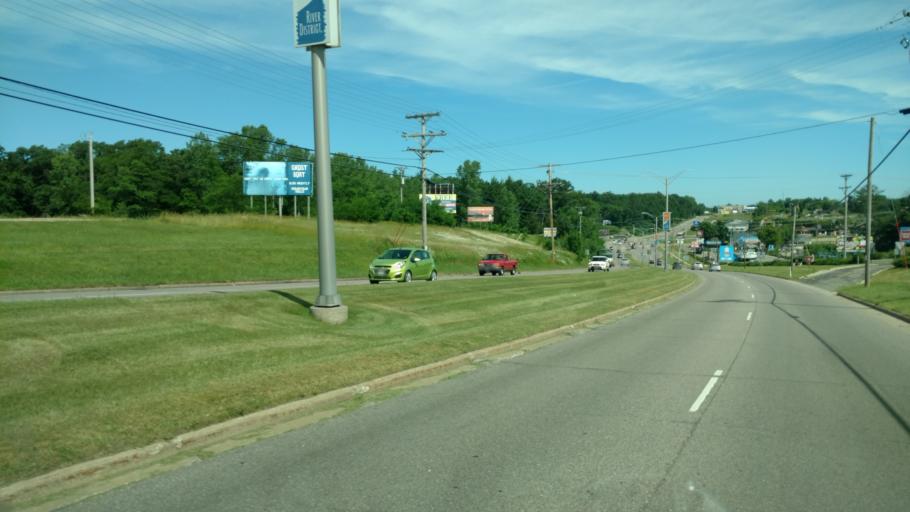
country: US
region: Wisconsin
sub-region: Columbia County
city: Wisconsin Dells
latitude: 43.6217
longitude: -89.7839
